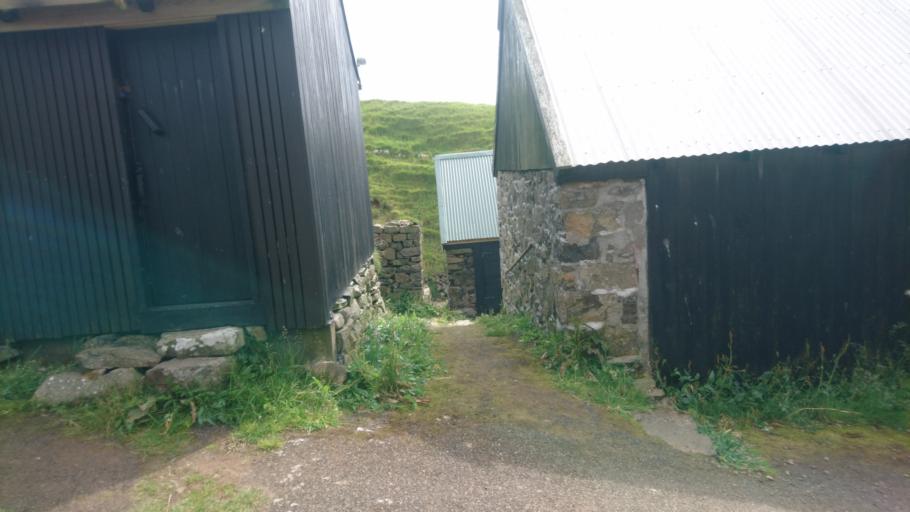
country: FO
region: Vagar
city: Sorvagur
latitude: 62.1037
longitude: -7.6436
